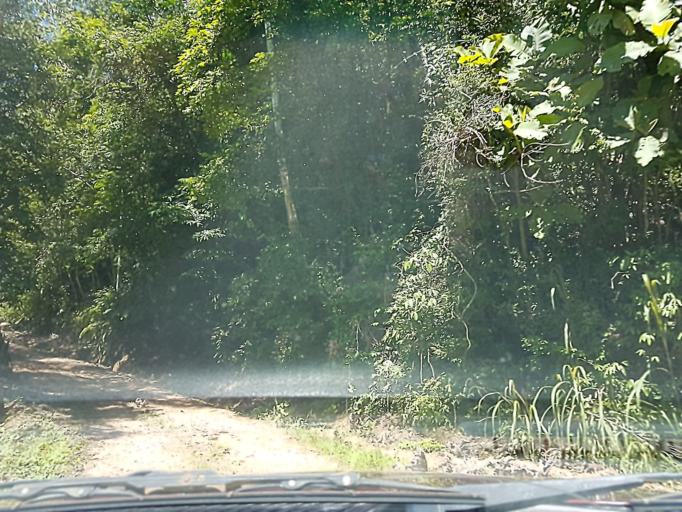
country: BR
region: Santa Catarina
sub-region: Braco Do Norte
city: Braco do Norte
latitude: -28.3873
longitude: -49.1245
